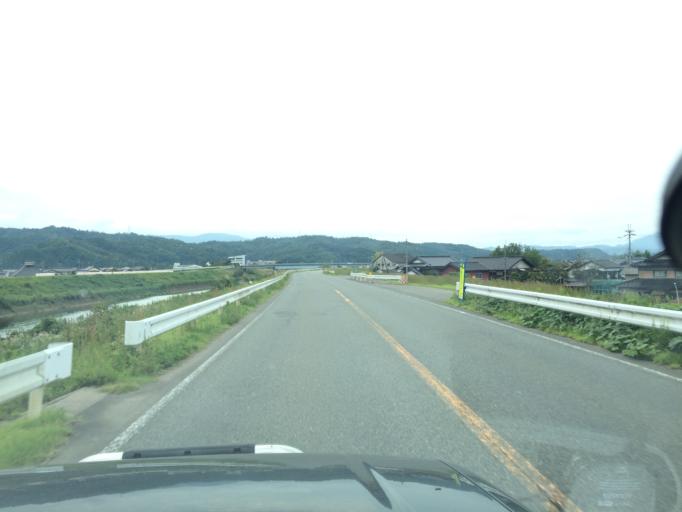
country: JP
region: Hyogo
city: Toyooka
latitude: 35.5100
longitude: 134.8307
